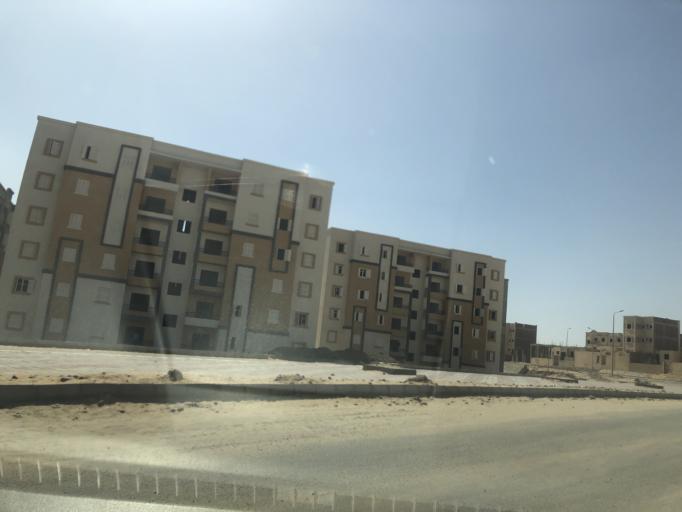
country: EG
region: Al Jizah
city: Madinat Sittah Uktubar
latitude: 29.9287
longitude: 31.0104
